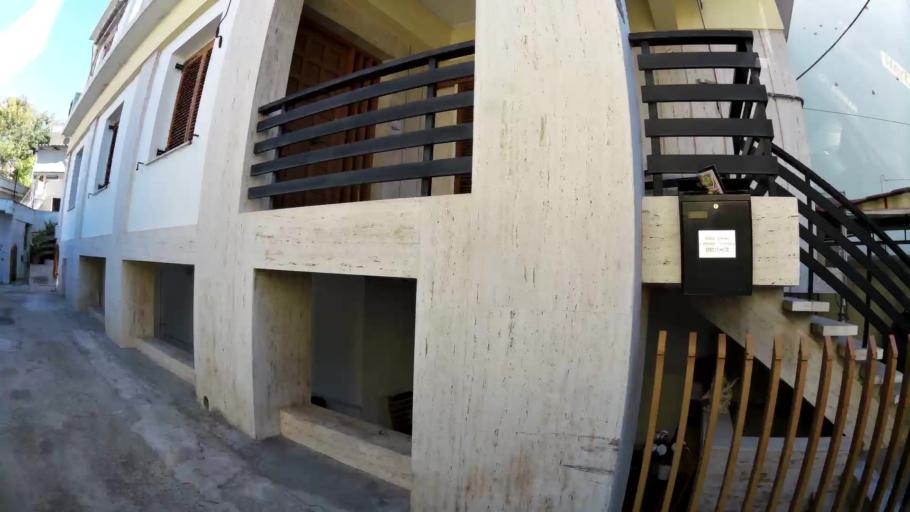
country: GR
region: Attica
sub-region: Nomarchia Athinas
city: Khalandrion
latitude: 38.0177
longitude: 23.7976
